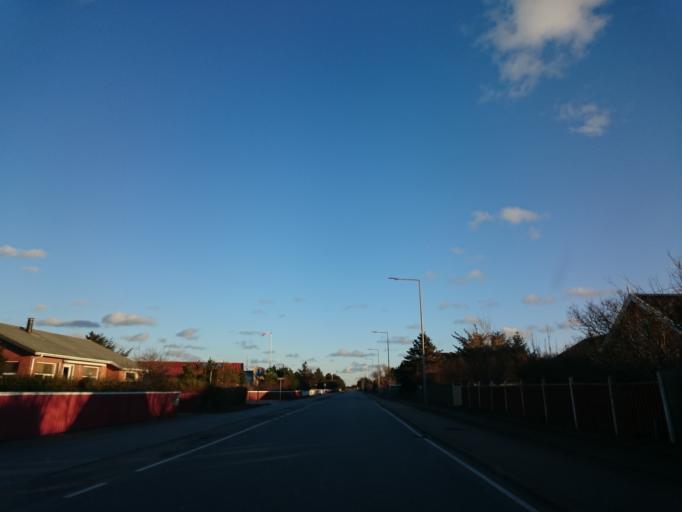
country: DK
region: North Denmark
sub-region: Frederikshavn Kommune
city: Skagen
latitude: 57.7276
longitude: 10.5384
